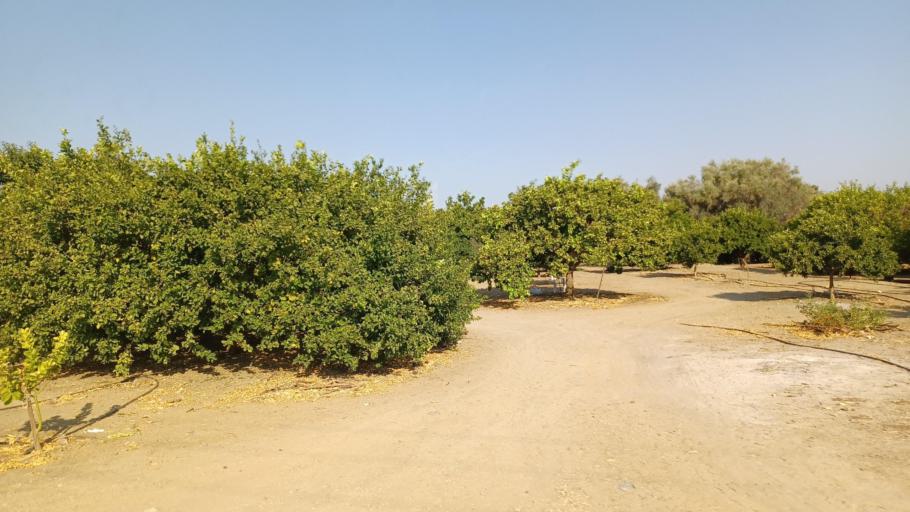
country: CY
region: Pafos
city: Polis
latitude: 35.0583
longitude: 32.4801
